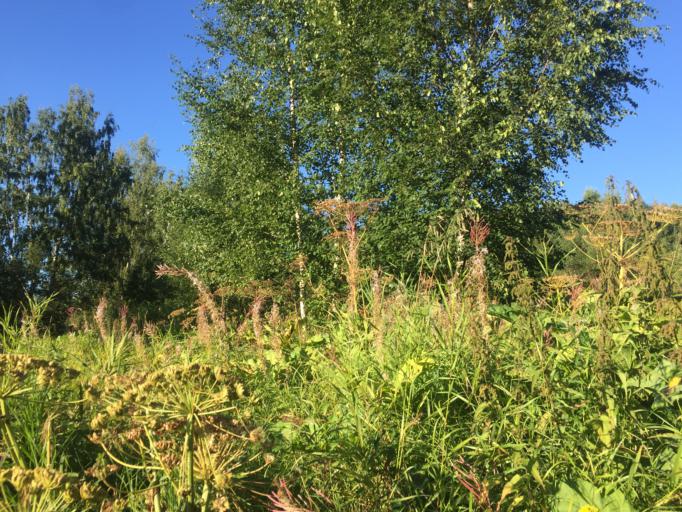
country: RU
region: Leningrad
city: Murino
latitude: 60.0412
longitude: 30.4572
